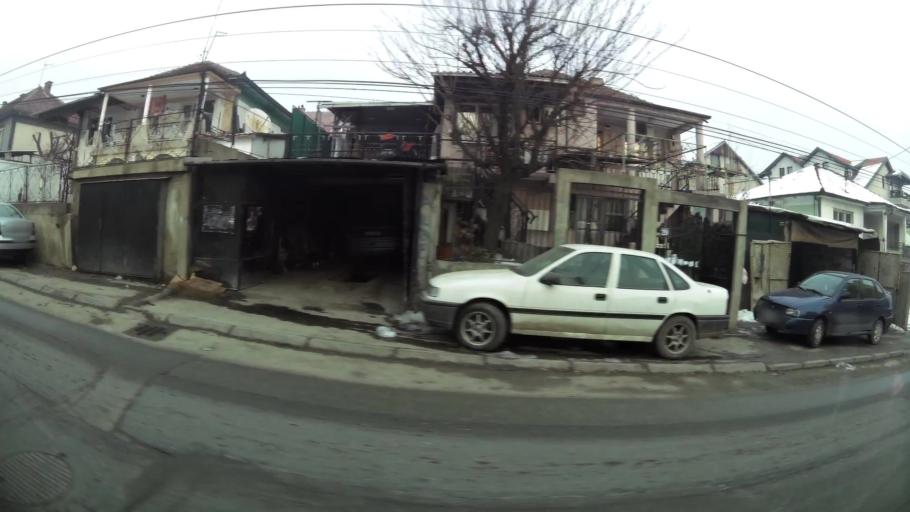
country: MK
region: Suto Orizari
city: Suto Orizare
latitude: 42.0349
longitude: 21.4265
